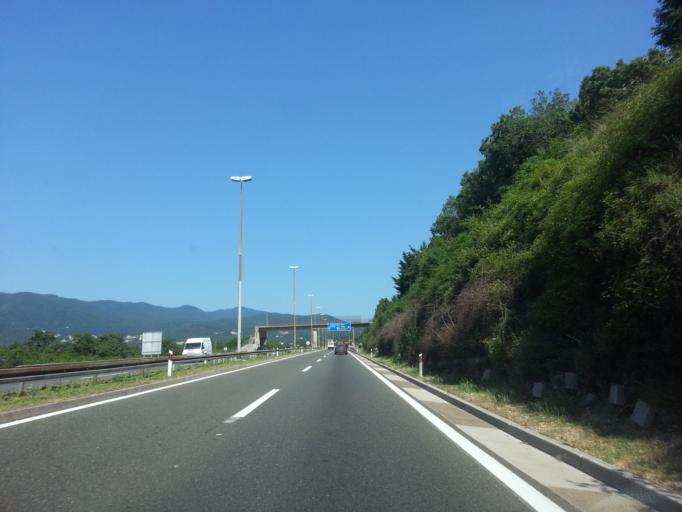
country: HR
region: Primorsko-Goranska
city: Rubesi
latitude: 45.3588
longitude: 14.3424
